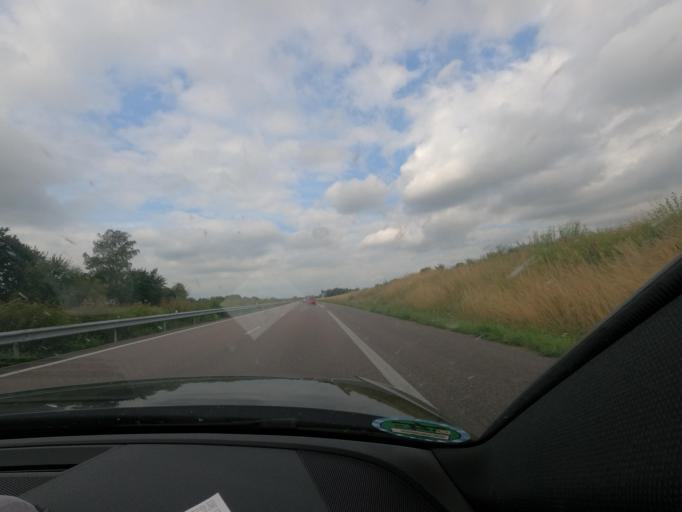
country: FR
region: Haute-Normandie
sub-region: Departement de la Seine-Maritime
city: Yvetot
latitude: 49.6434
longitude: 0.7556
